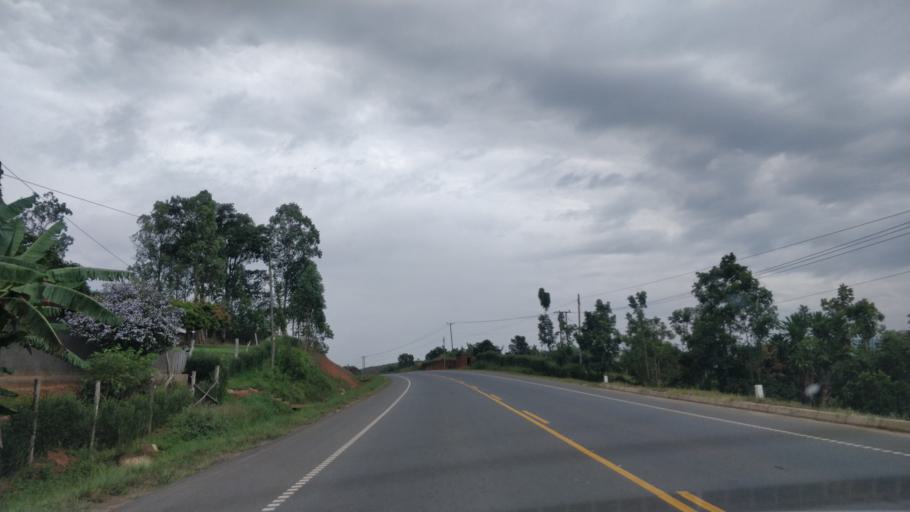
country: UG
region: Western Region
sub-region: Sheema District
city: Kibingo
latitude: -0.6557
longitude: 30.4797
